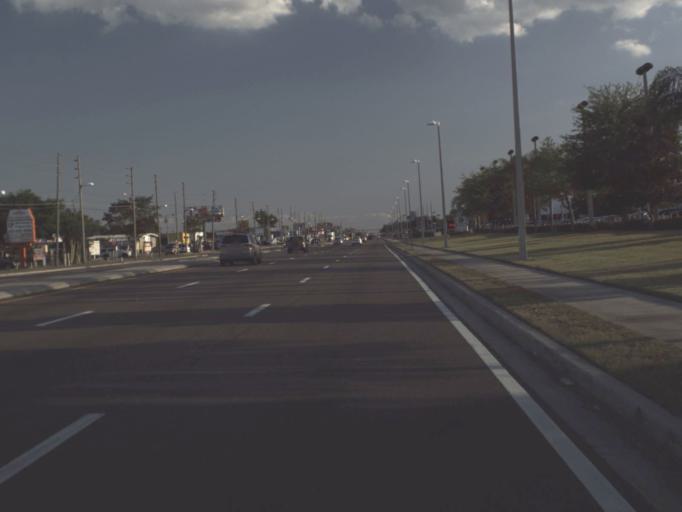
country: US
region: Florida
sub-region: Orange County
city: Southchase
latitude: 28.4155
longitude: -81.4048
